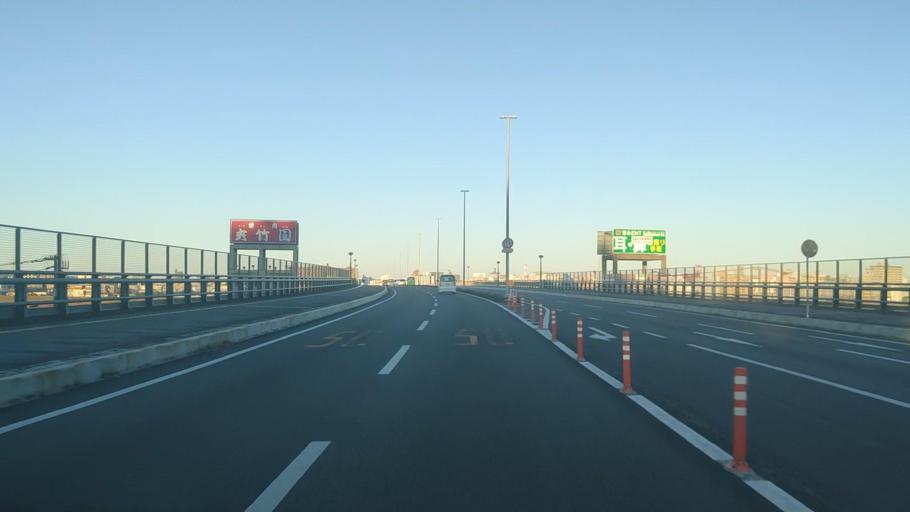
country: JP
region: Miyazaki
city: Miyazaki-shi
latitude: 31.9056
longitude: 131.4092
